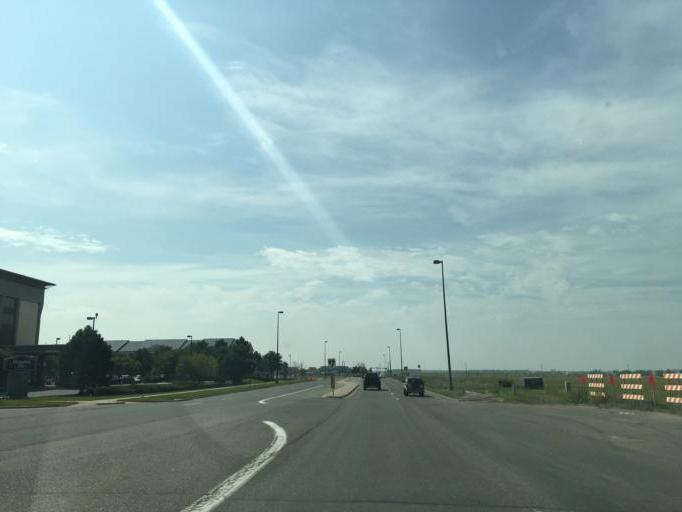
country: US
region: Colorado
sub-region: Adams County
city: Aurora
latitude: 39.8115
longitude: -104.7722
